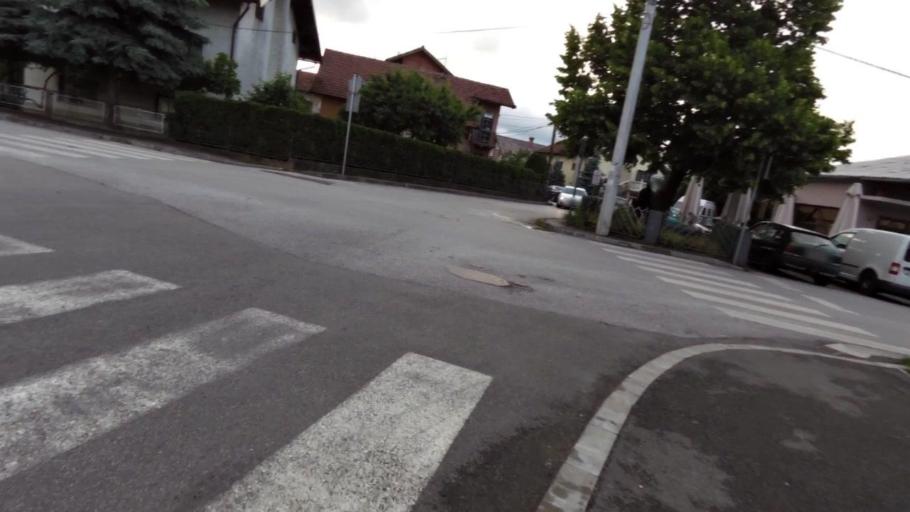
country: HR
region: Grad Zagreb
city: Dubrava
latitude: 45.8415
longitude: 16.0516
